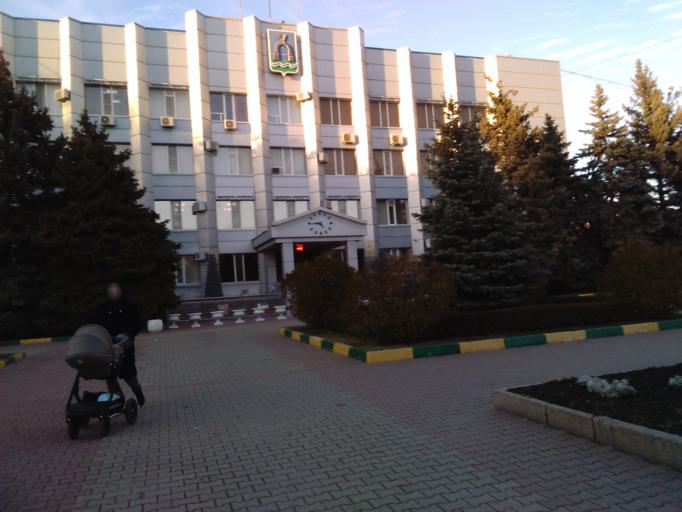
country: RU
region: Rostov
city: Bataysk
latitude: 47.1384
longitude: 39.7448
